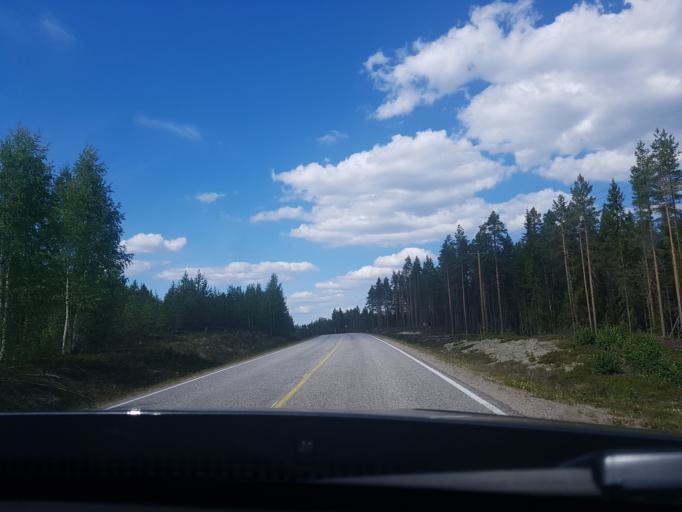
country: FI
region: Kainuu
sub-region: Kehys-Kainuu
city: Kuhmo
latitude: 64.2395
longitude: 29.8145
